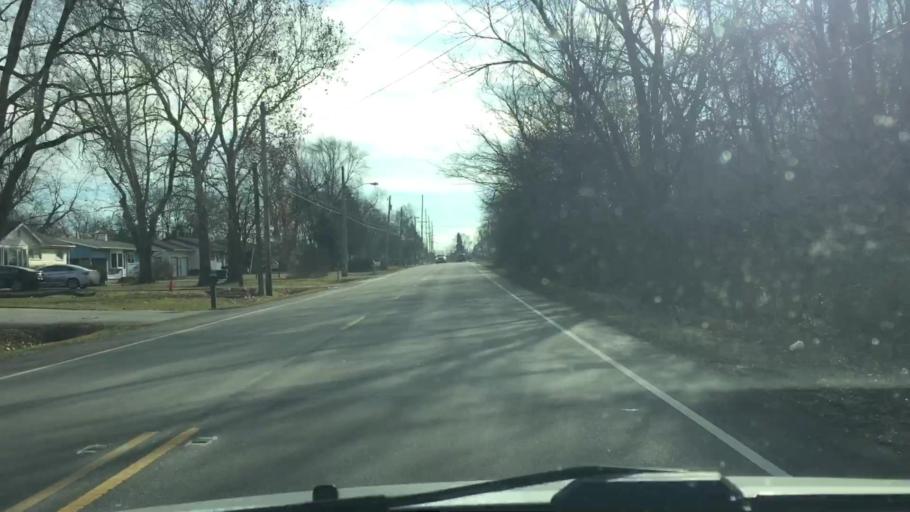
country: US
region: Illinois
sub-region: Kane County
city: Batavia
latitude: 41.8647
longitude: -88.3066
